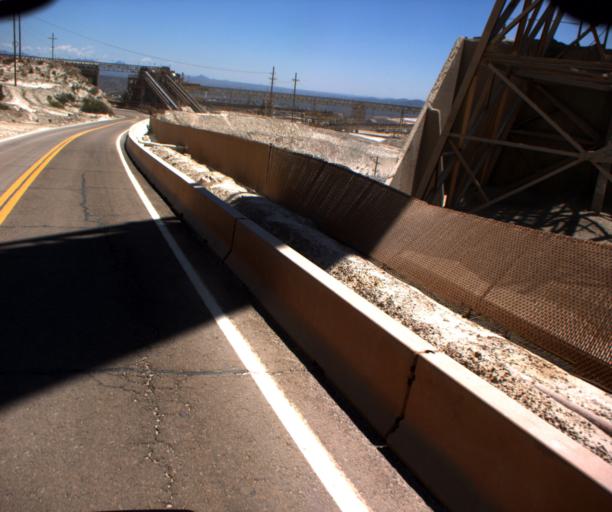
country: US
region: Arizona
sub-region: Greenlee County
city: Morenci
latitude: 33.0698
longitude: -109.3476
